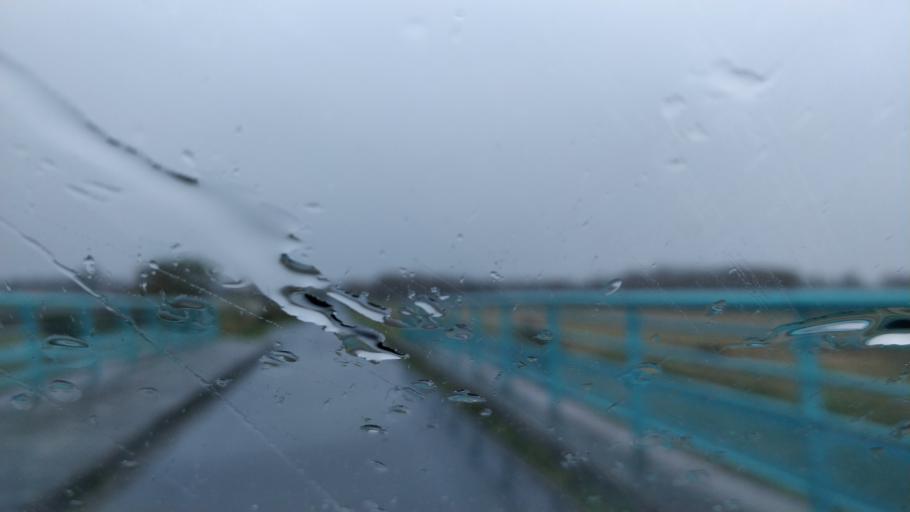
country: FR
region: Lower Normandy
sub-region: Departement de la Manche
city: Brehal
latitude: 48.9016
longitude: -1.5549
